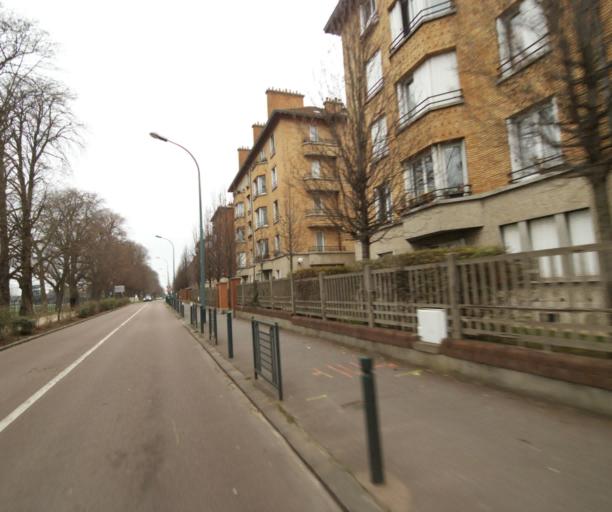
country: FR
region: Ile-de-France
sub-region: Departement des Hauts-de-Seine
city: Saint-Cloud
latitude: 48.8604
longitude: 2.2047
